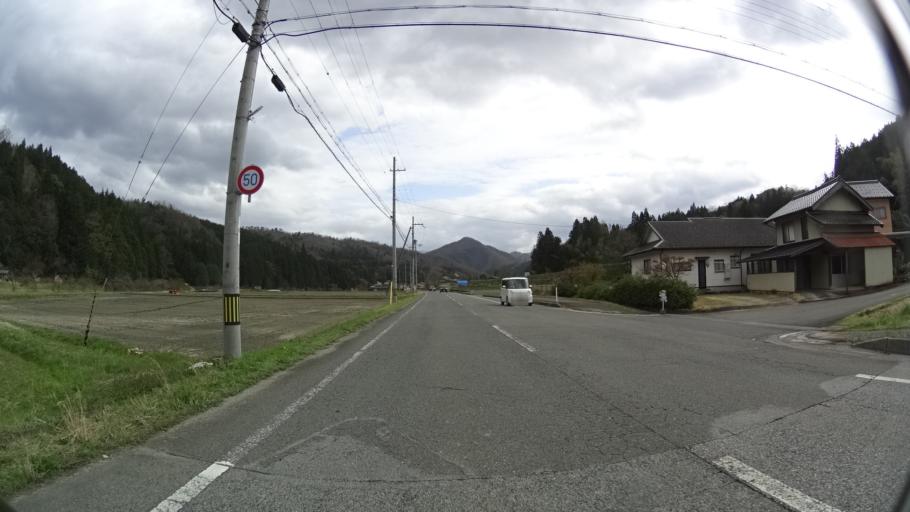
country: JP
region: Hyogo
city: Toyooka
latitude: 35.4773
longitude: 134.9276
